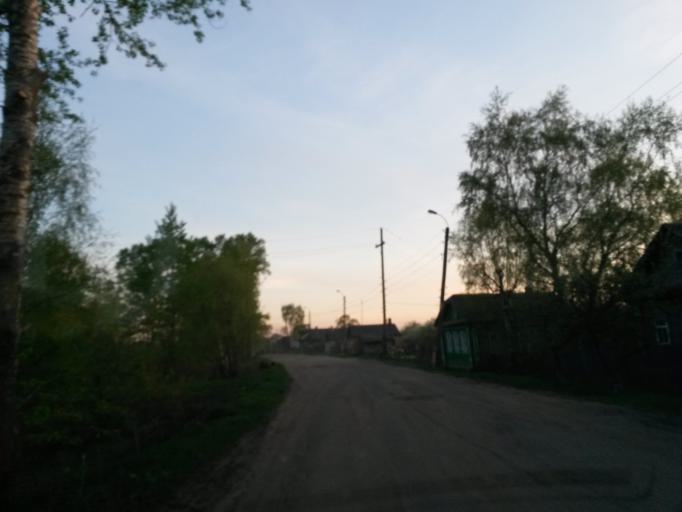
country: RU
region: Jaroslavl
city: Tutayev
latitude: 57.8882
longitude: 39.5532
